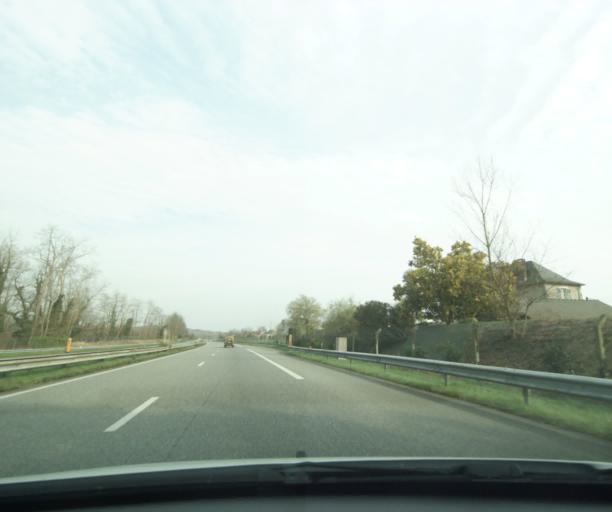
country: FR
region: Aquitaine
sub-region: Departement des Pyrenees-Atlantiques
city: Orthez
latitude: 43.4586
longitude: -0.7155
